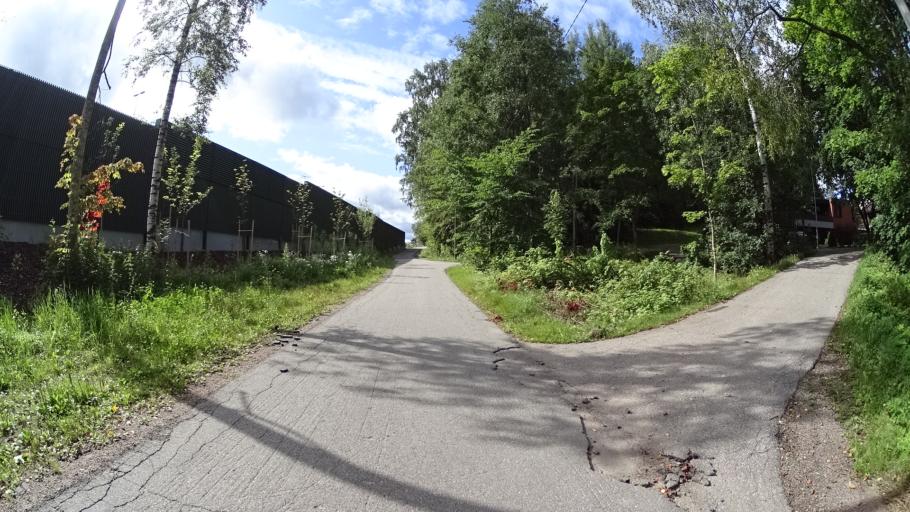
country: FI
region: Uusimaa
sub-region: Helsinki
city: Teekkarikylae
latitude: 60.2302
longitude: 24.8390
